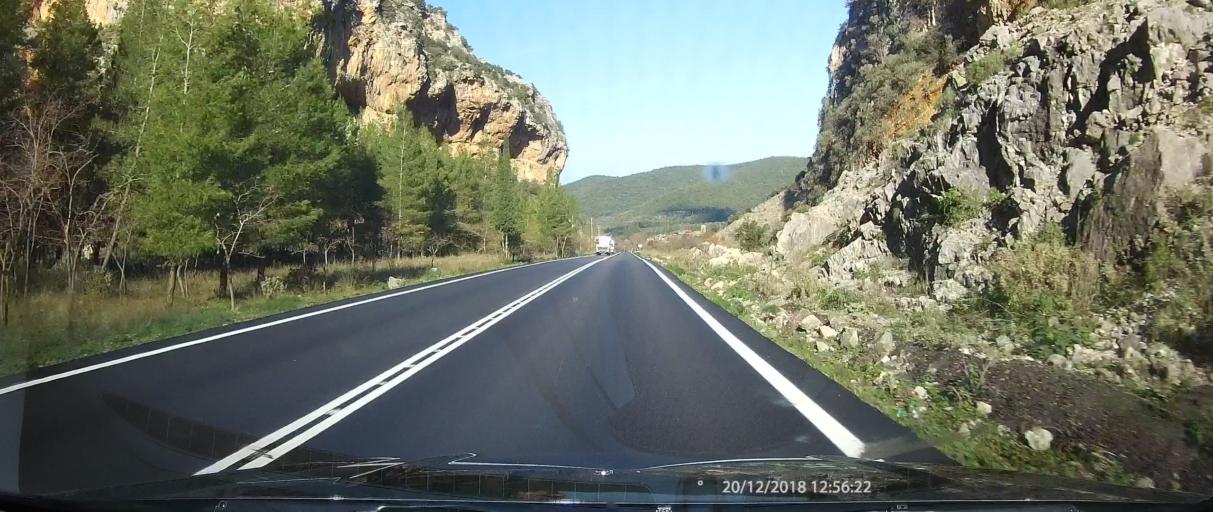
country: GR
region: West Greece
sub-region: Nomos Aitolias kai Akarnanias
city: Pappadhatai
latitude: 38.5096
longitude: 21.3789
